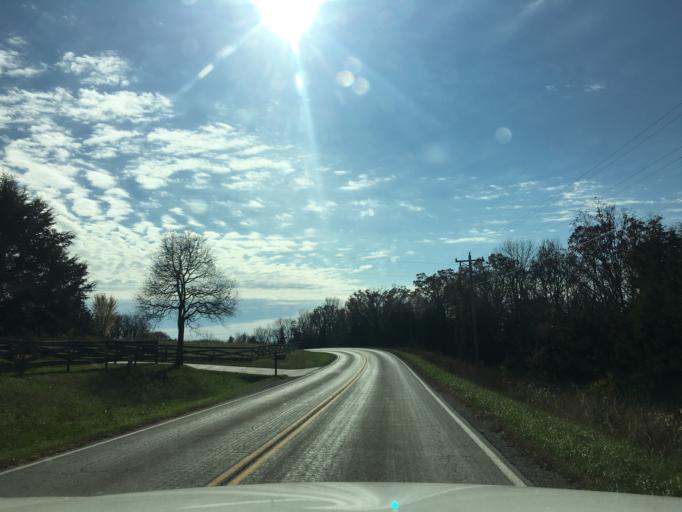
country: US
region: Missouri
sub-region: Osage County
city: Linn
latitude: 38.4503
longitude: -91.8380
